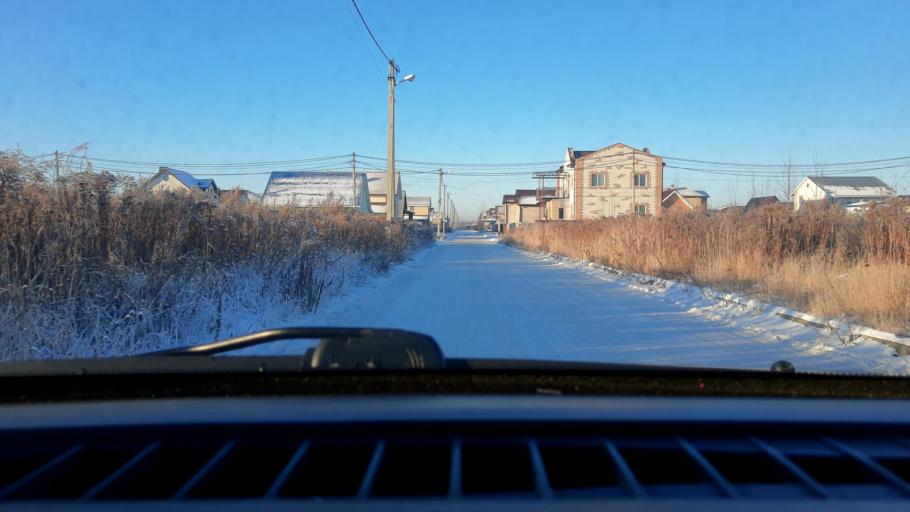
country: RU
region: Nizjnij Novgorod
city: Bor
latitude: 56.3892
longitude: 44.0659
